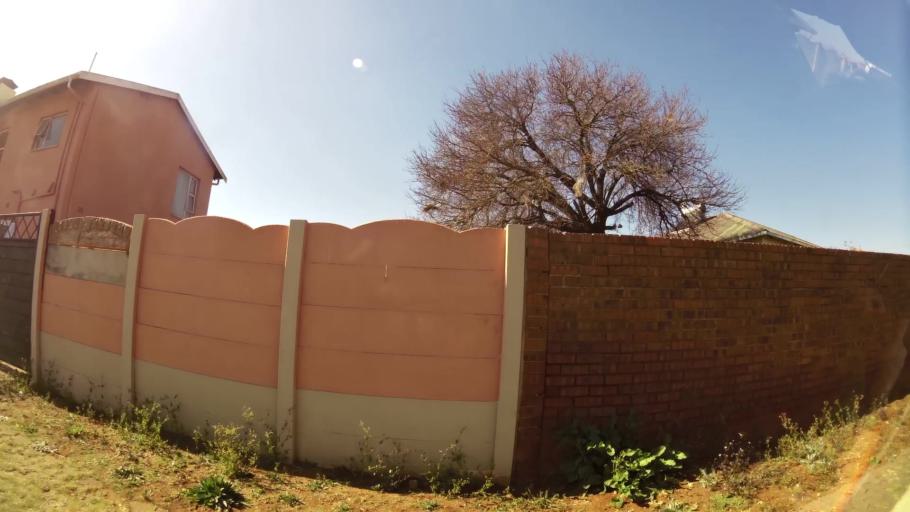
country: ZA
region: Gauteng
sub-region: City of Johannesburg Metropolitan Municipality
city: Johannesburg
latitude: -26.1877
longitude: 27.9788
